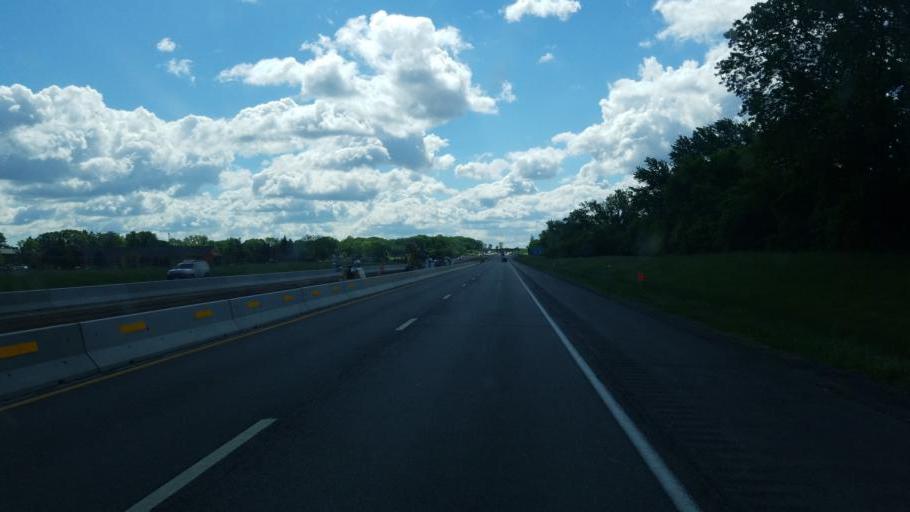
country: US
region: New York
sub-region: Onondaga County
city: Galeville
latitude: 43.1066
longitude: -76.1921
